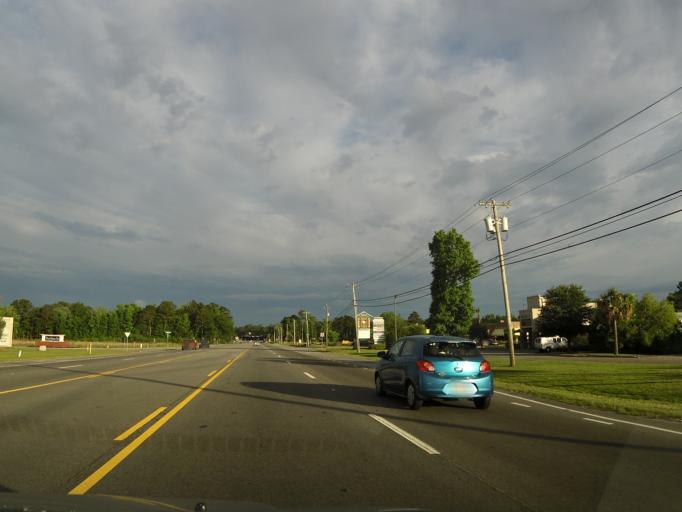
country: US
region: Georgia
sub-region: Chatham County
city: Pooler
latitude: 32.1039
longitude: -81.2258
